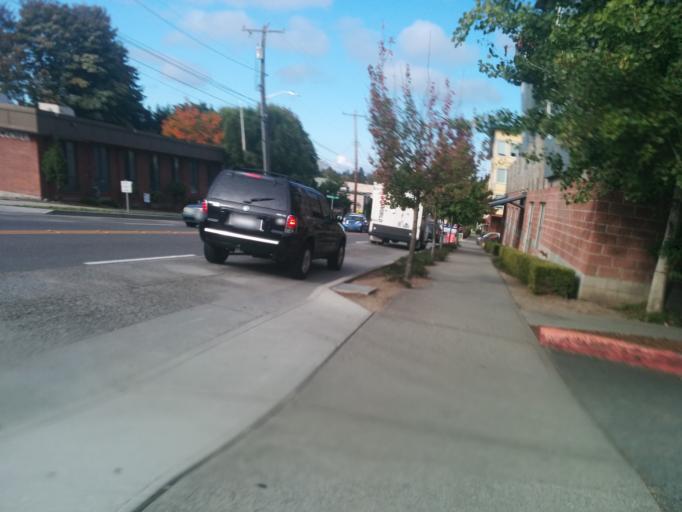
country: US
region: Washington
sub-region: King County
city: Shoreline
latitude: 47.6905
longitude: -122.3504
